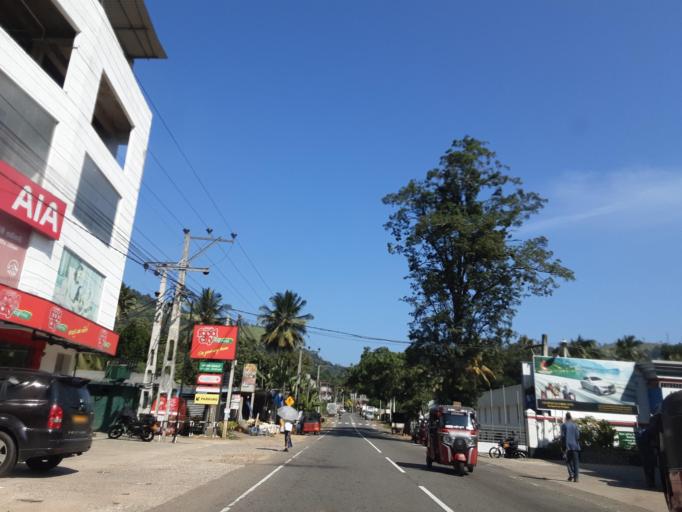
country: LK
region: Uva
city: Badulla
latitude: 6.9984
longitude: 81.0570
